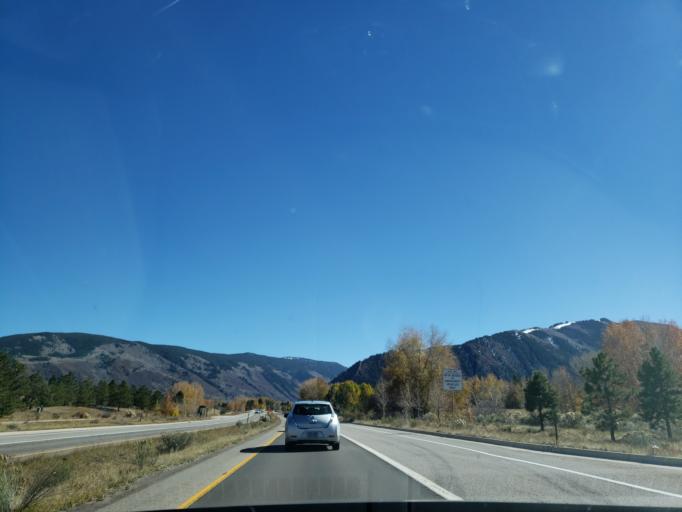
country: US
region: Colorado
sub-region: Pitkin County
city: Aspen
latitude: 39.2037
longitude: -106.8548
